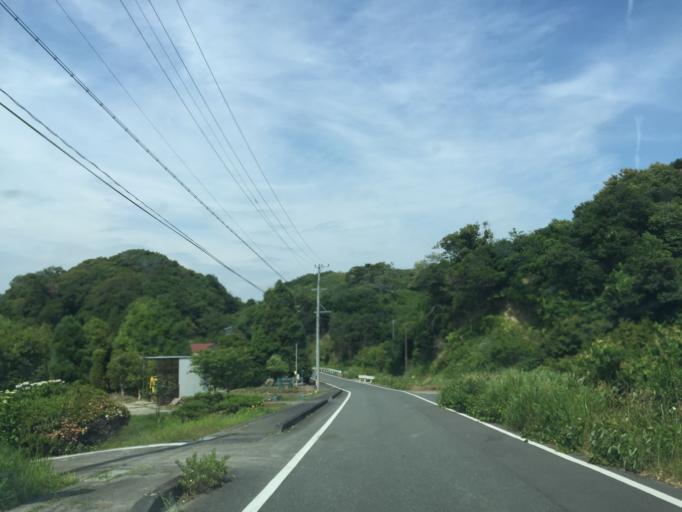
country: JP
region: Shizuoka
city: Kakegawa
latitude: 34.7547
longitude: 138.0066
